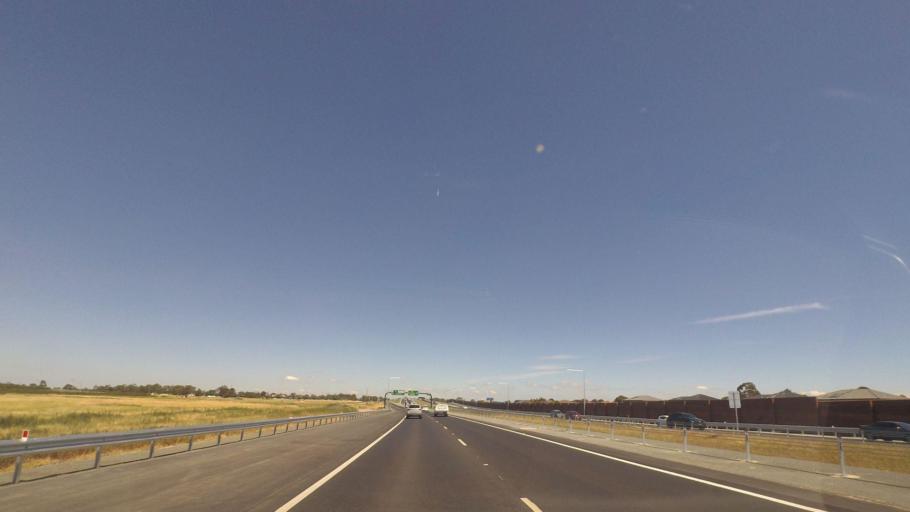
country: AU
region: Victoria
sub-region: Kingston
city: Waterways
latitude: -38.0198
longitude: 145.1278
